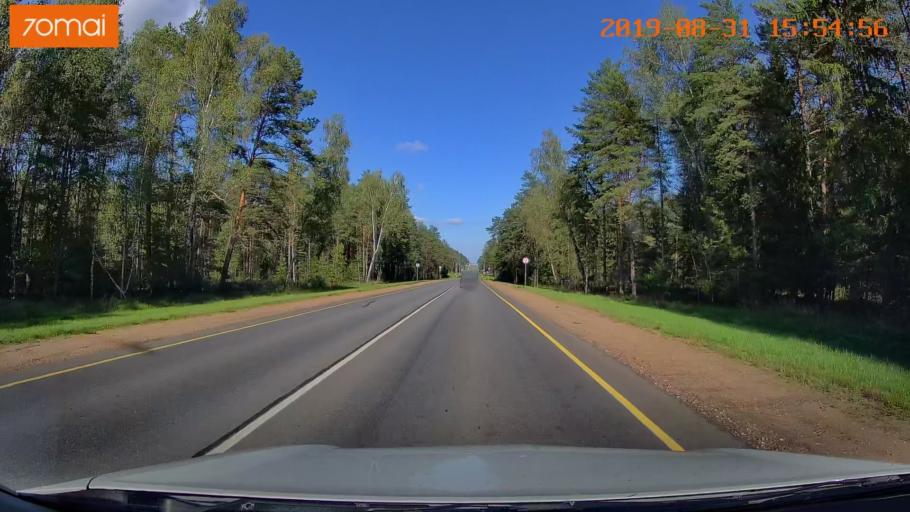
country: RU
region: Kaluga
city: Yukhnov
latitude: 54.7222
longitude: 35.1609
